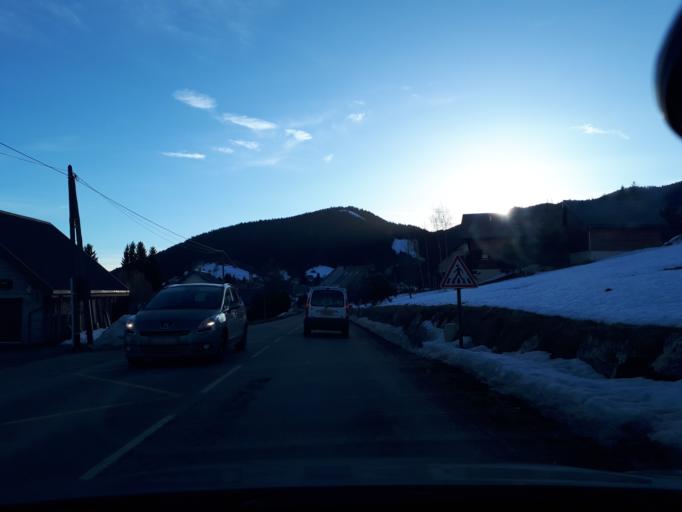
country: FR
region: Rhone-Alpes
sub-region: Departement de l'Isere
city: Meaudre
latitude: 45.1339
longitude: 5.5315
